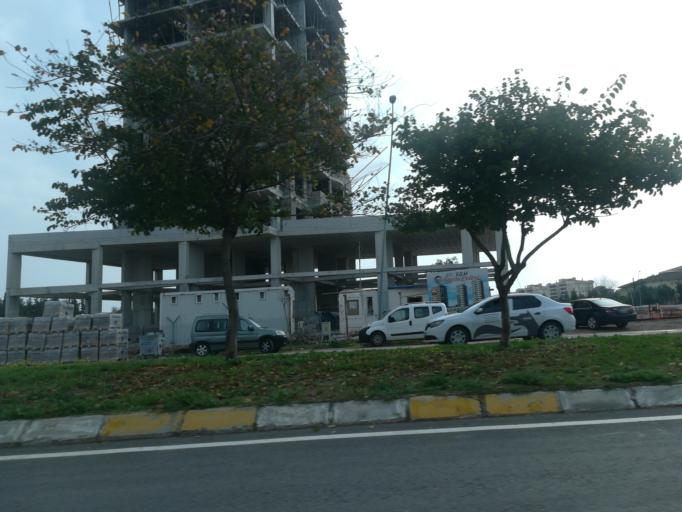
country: TR
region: Adana
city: Yuregir
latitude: 36.9869
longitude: 35.3674
